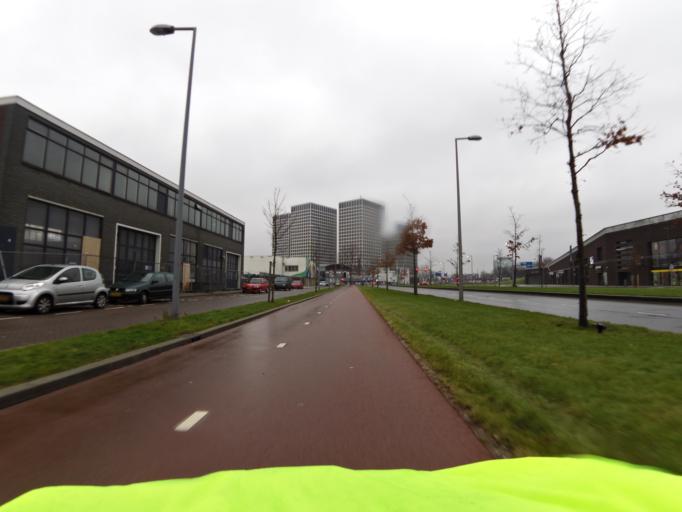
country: NL
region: South Holland
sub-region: Gemeente Rotterdam
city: Delfshaven
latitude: 51.9095
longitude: 4.4353
